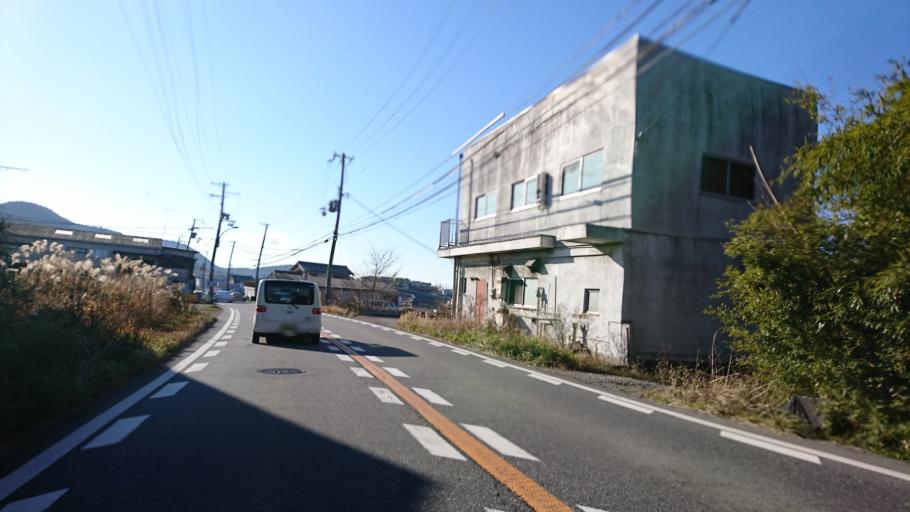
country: JP
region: Hyogo
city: Kakogawacho-honmachi
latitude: 34.8177
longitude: 134.8351
